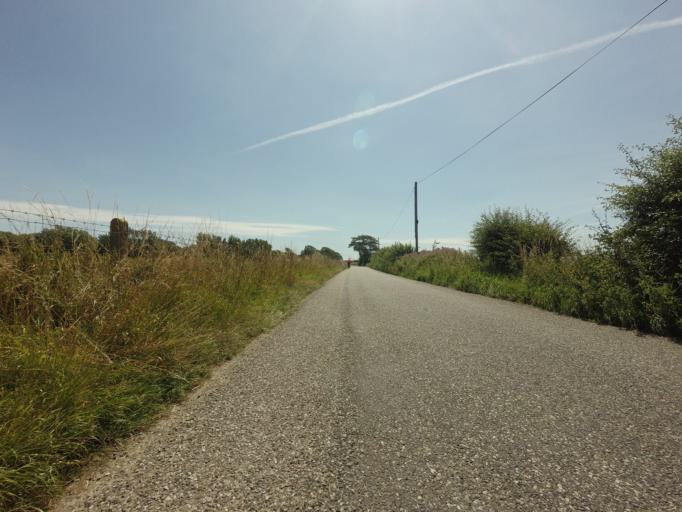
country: GB
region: England
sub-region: Kent
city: Lydd
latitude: 50.9614
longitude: 0.9030
